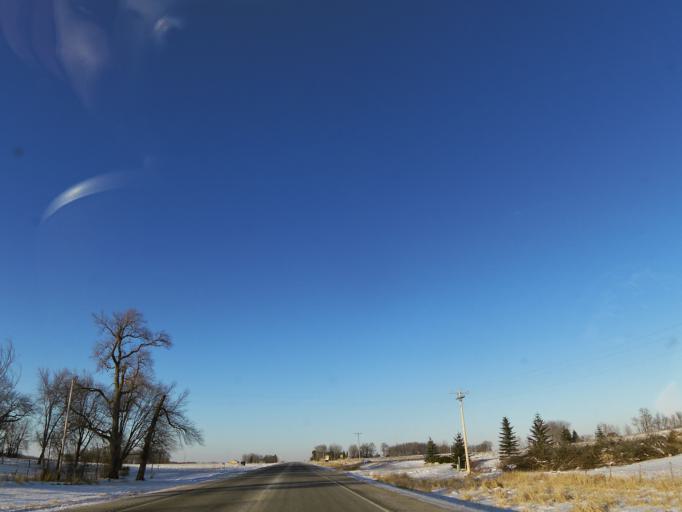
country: US
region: Minnesota
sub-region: Rice County
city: Lonsdale
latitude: 44.5165
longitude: -93.4429
